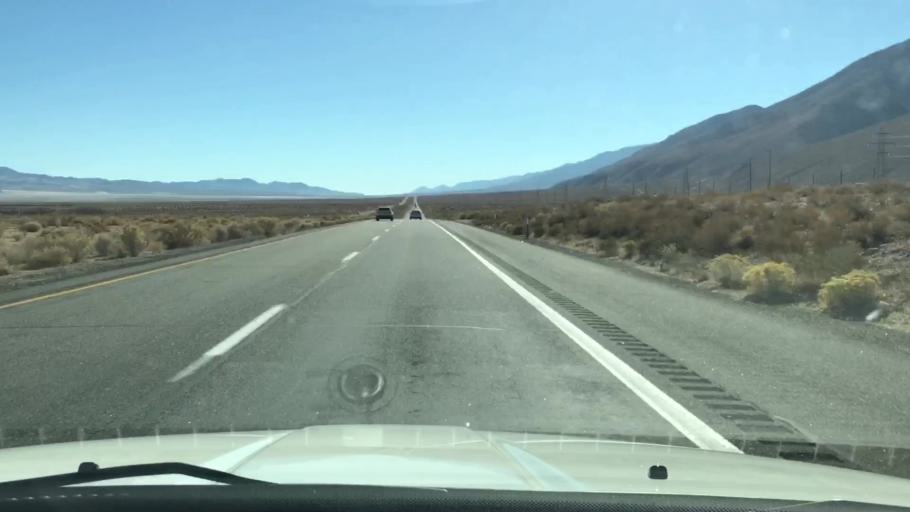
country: US
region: California
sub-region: Inyo County
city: Lone Pine
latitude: 36.4310
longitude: -118.0318
